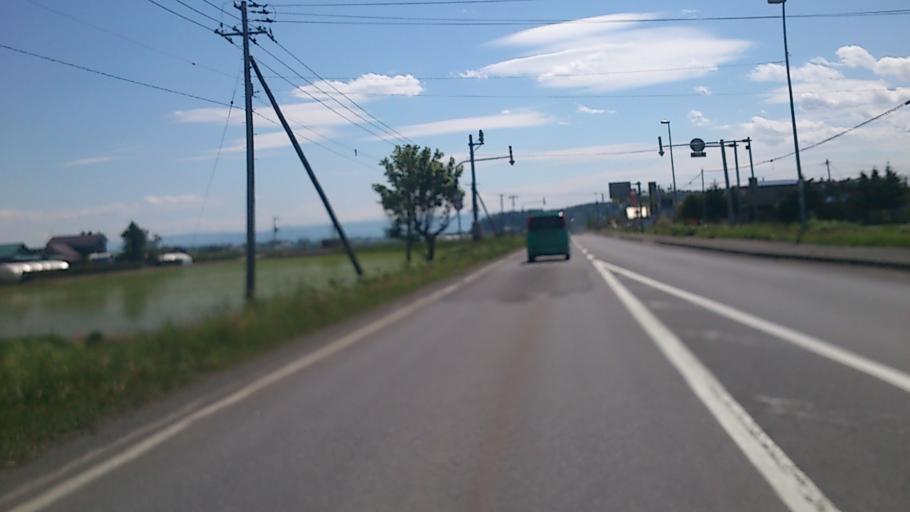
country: JP
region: Hokkaido
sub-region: Asahikawa-shi
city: Asahikawa
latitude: 43.8669
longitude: 142.4834
